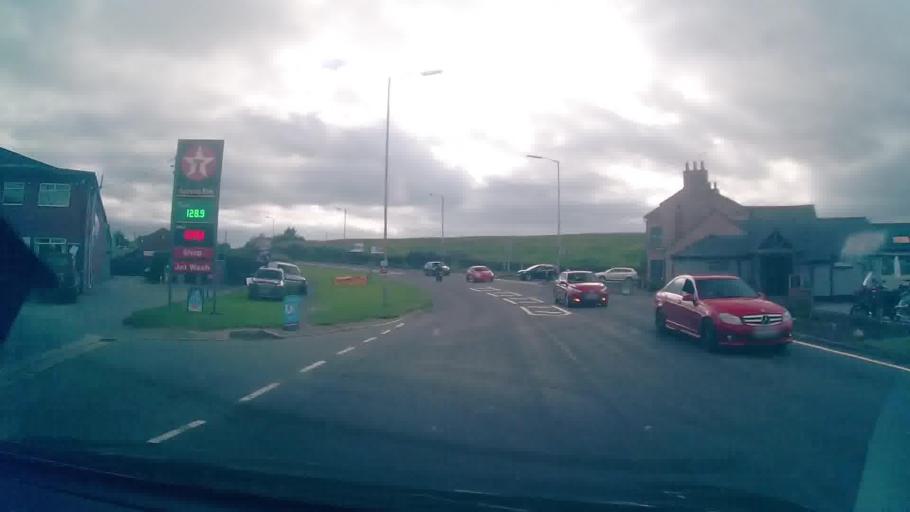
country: GB
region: England
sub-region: Shropshire
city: Whitchurch
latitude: 52.9845
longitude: -2.7135
